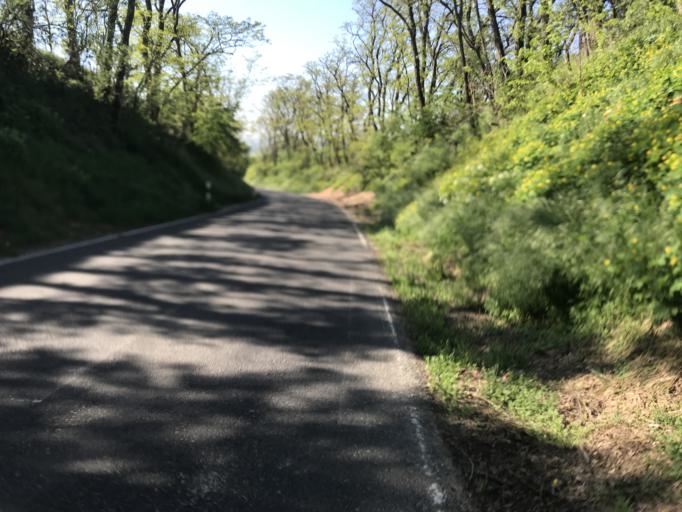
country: DE
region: Rheinland-Pfalz
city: Zornheim
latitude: 49.8775
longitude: 8.2161
